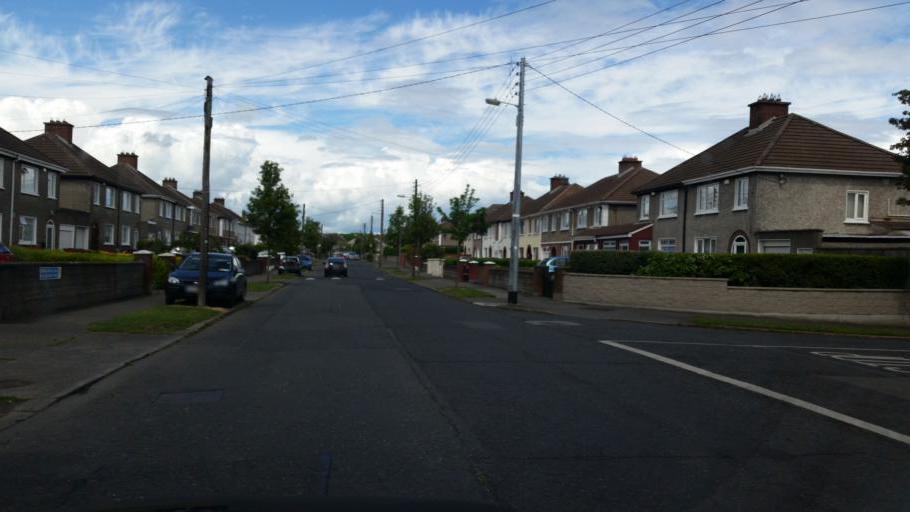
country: IE
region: Leinster
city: Ballymun
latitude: 53.3916
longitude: -6.2794
